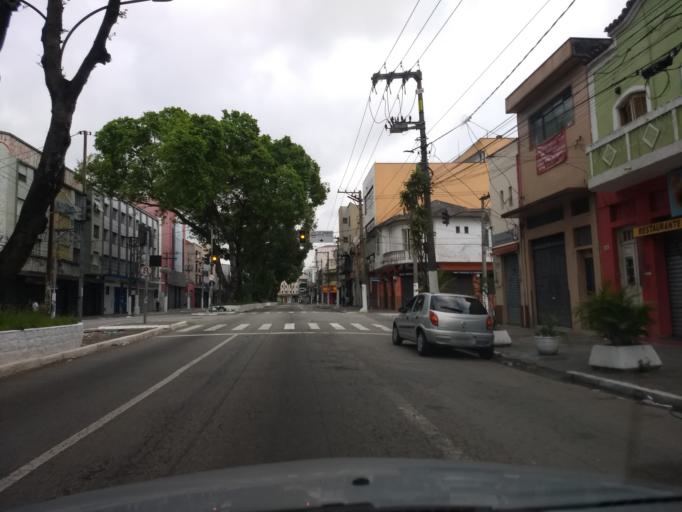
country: BR
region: Sao Paulo
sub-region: Sao Paulo
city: Sao Paulo
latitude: -23.5297
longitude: -46.6146
